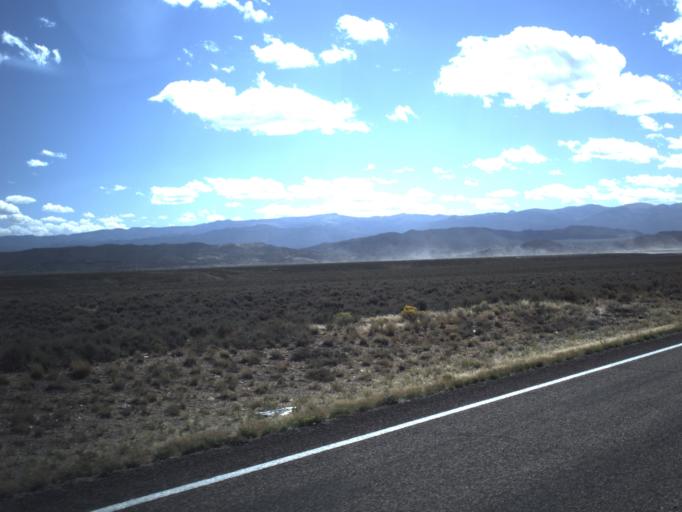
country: US
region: Utah
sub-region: Iron County
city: Enoch
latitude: 37.9704
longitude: -113.0062
